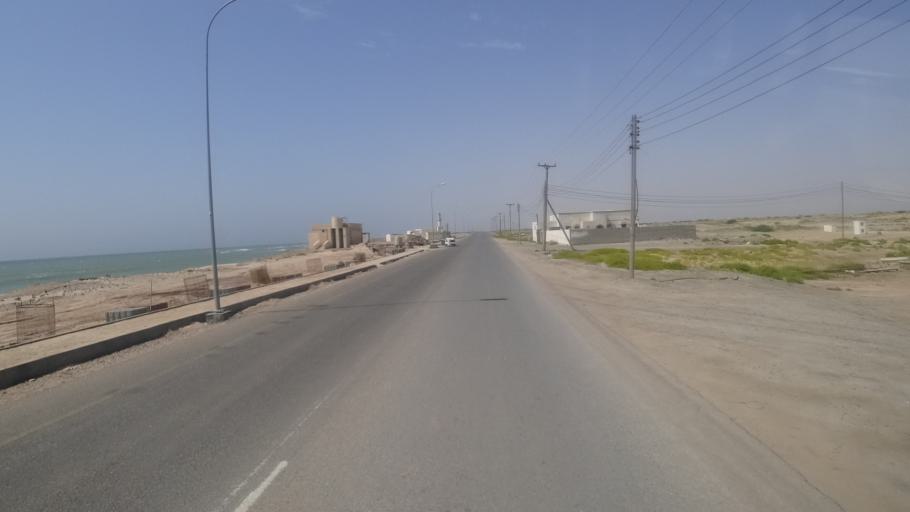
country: OM
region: Ash Sharqiyah
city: Sur
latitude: 22.1132
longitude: 59.7115
